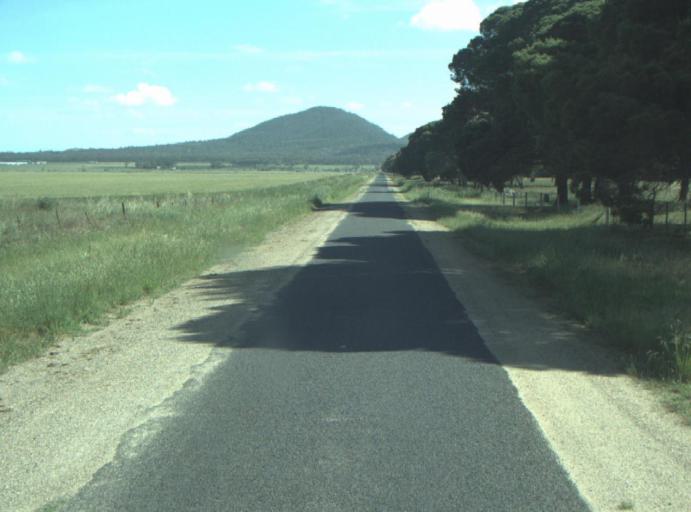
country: AU
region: Victoria
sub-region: Greater Geelong
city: Lara
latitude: -37.9953
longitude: 144.4201
